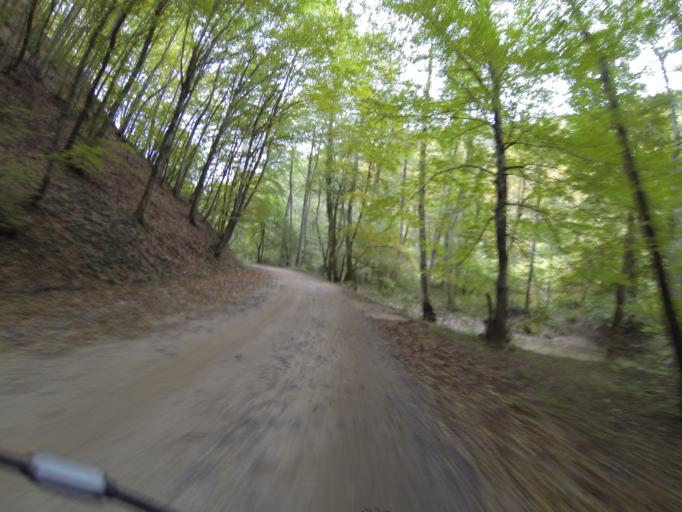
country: RO
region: Gorj
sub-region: Comuna Tismana
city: Pocruia
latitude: 45.0547
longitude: 22.9075
